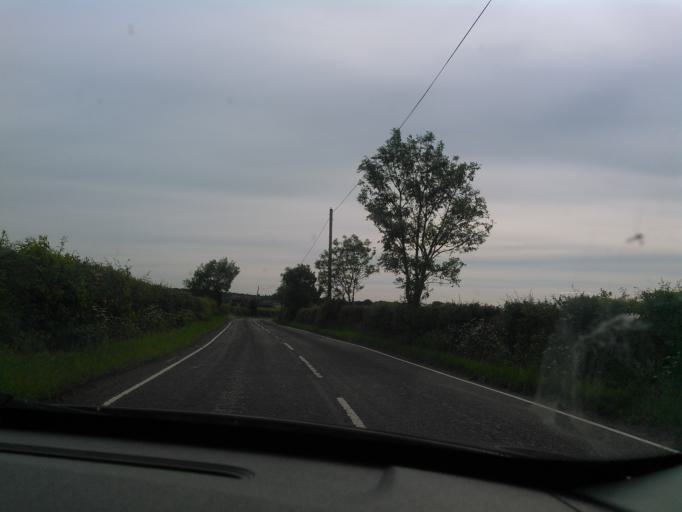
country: GB
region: England
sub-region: Shropshire
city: Shawbury
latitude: 52.7435
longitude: -2.6442
